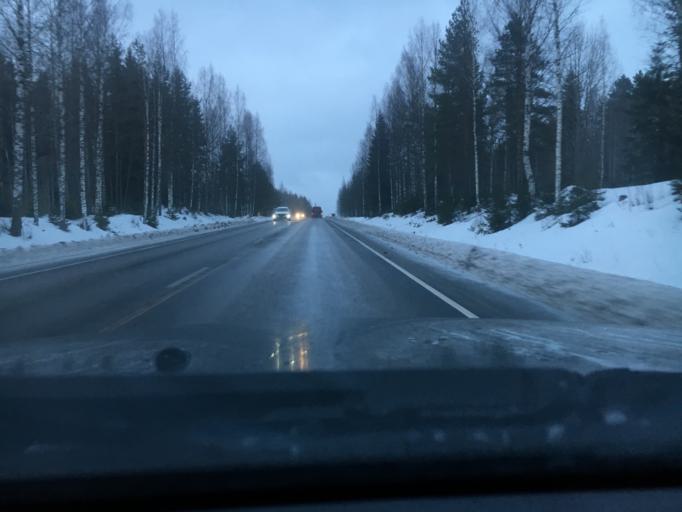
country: FI
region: Central Finland
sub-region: Jyvaeskylae
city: Hankasalmi
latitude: 62.3957
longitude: 26.6431
